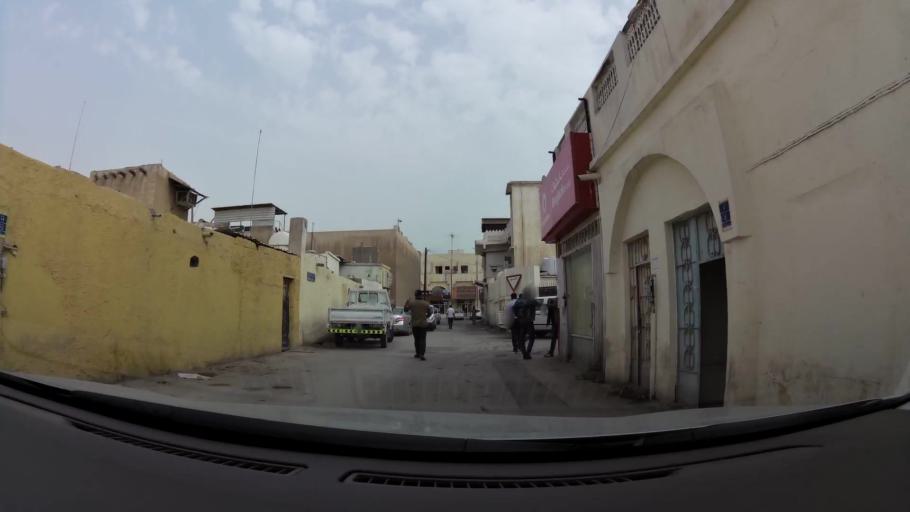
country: QA
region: Baladiyat ad Dawhah
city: Doha
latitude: 25.2690
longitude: 51.5397
